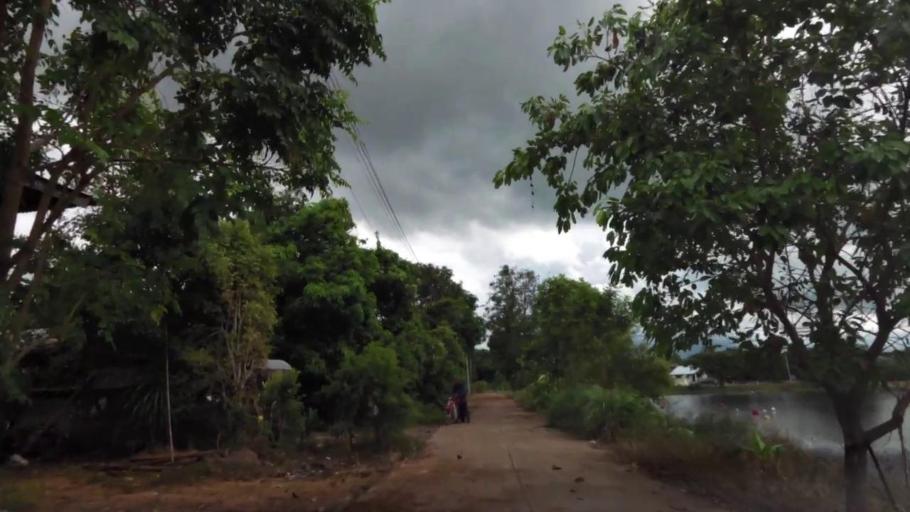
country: TH
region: Nakhon Sawan
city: Phai Sali
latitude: 15.6077
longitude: 100.6546
